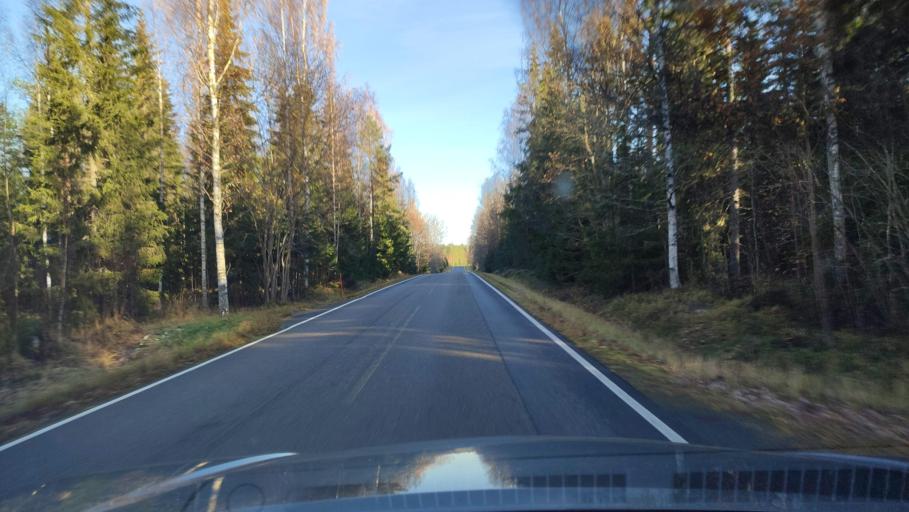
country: FI
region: Southern Ostrobothnia
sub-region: Suupohja
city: Teuva
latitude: 62.4102
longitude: 21.6976
